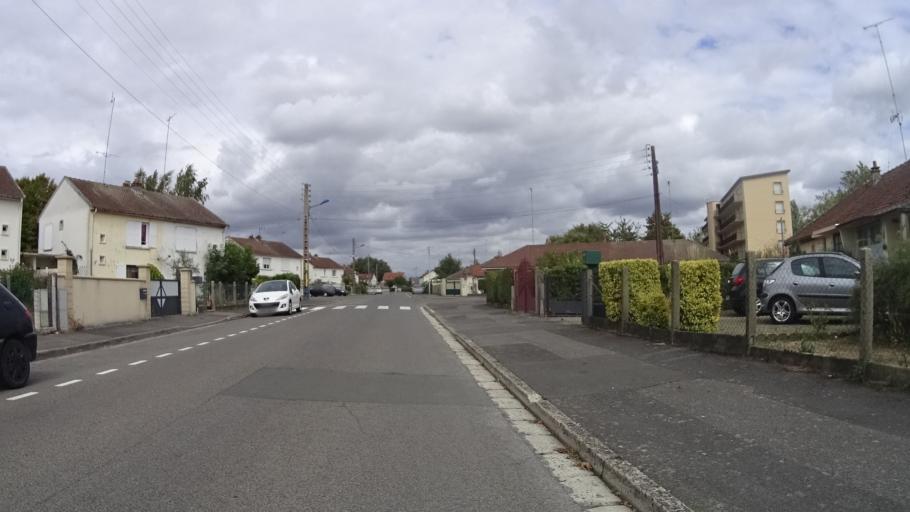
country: FR
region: Picardie
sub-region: Departement de l'Aisne
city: Beautor
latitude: 49.6529
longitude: 3.3436
